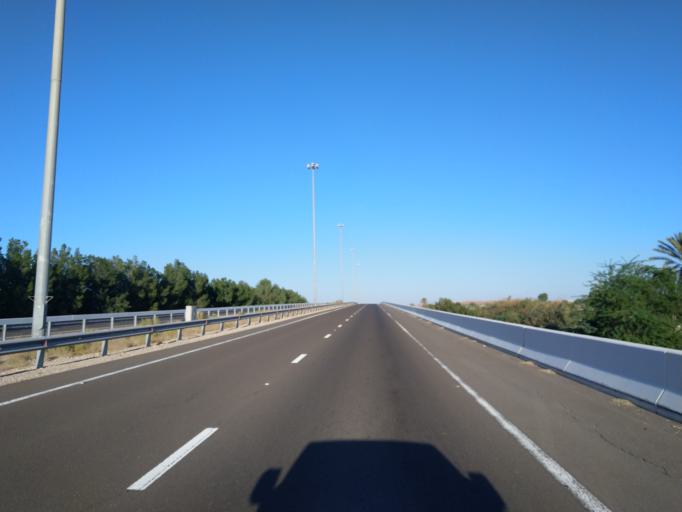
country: OM
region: Al Buraimi
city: Al Buraymi
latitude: 24.5494
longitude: 55.6755
